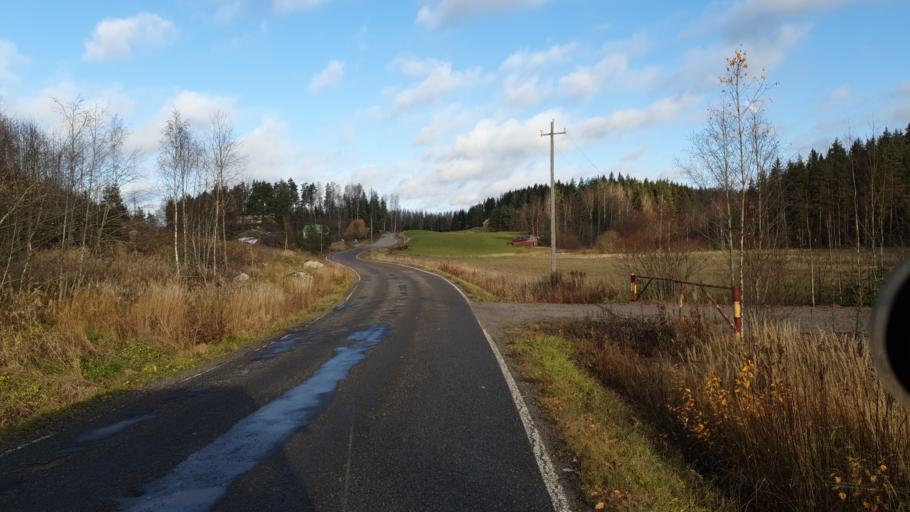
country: FI
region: Uusimaa
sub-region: Helsinki
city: Siuntio
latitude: 60.2662
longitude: 24.3043
